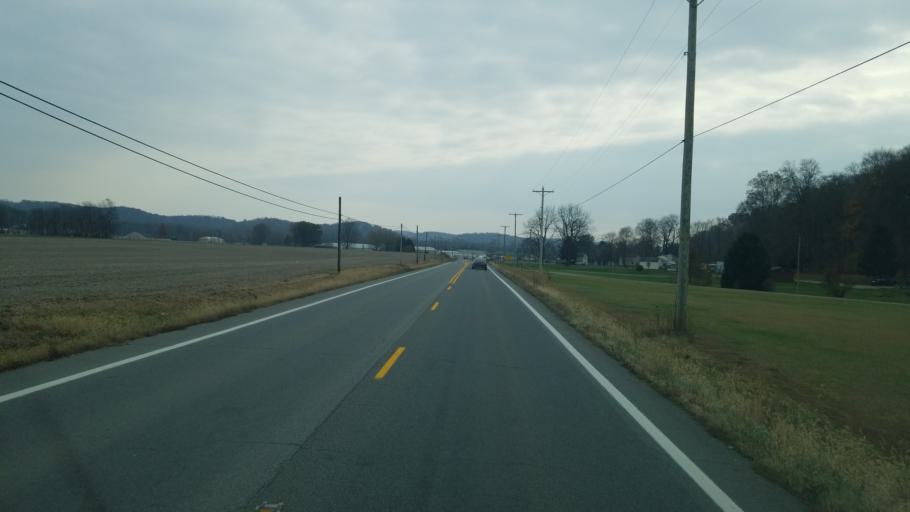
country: US
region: Ohio
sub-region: Licking County
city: Utica
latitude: 40.1886
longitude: -82.4264
